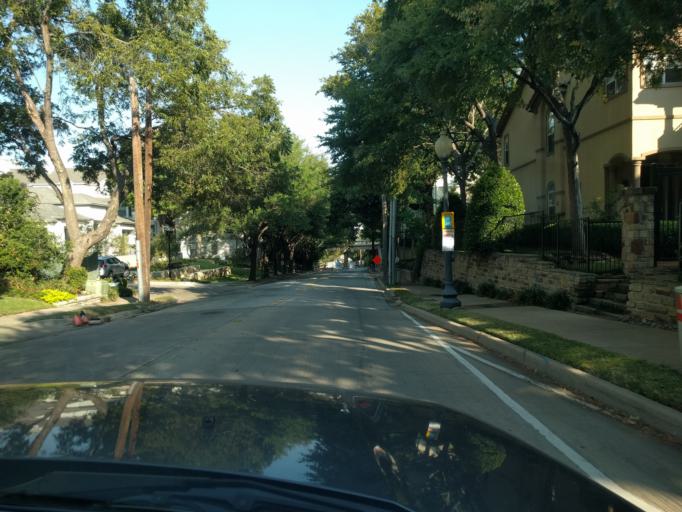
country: US
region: Texas
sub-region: Dallas County
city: Highland Park
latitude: 32.8109
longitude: -96.7983
